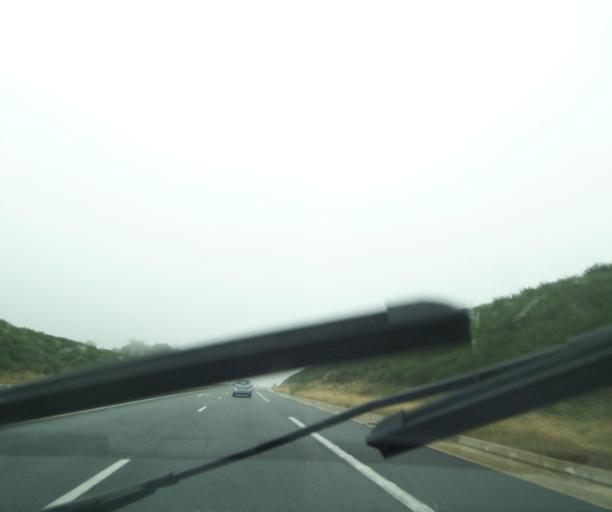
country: FR
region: Midi-Pyrenees
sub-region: Departement de l'Aveyron
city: Baraqueville
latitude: 44.2194
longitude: 2.4070
